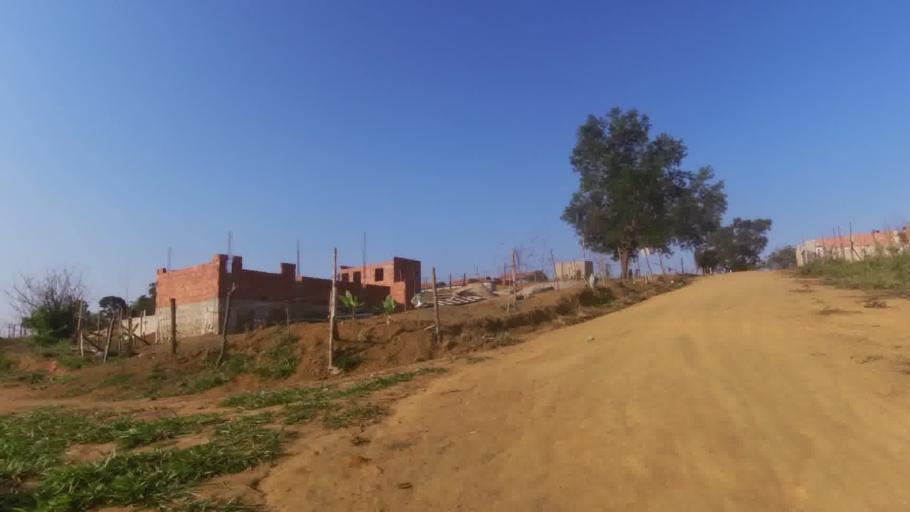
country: BR
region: Espirito Santo
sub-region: Piuma
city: Piuma
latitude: -20.8269
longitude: -40.7231
